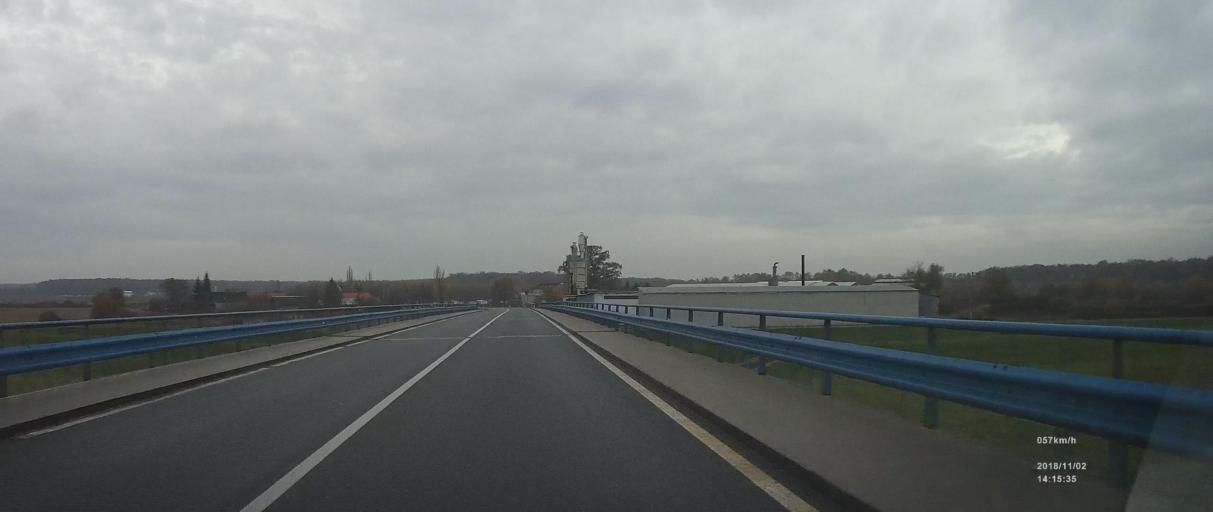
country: HR
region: Zagrebacka
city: Gradici
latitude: 45.6867
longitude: 16.0572
